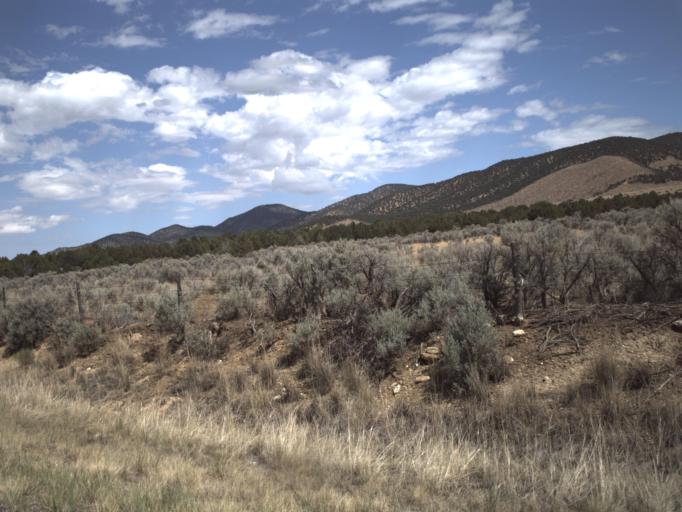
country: US
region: Utah
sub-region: Sanpete County
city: Centerfield
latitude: 39.1265
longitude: -112.0542
